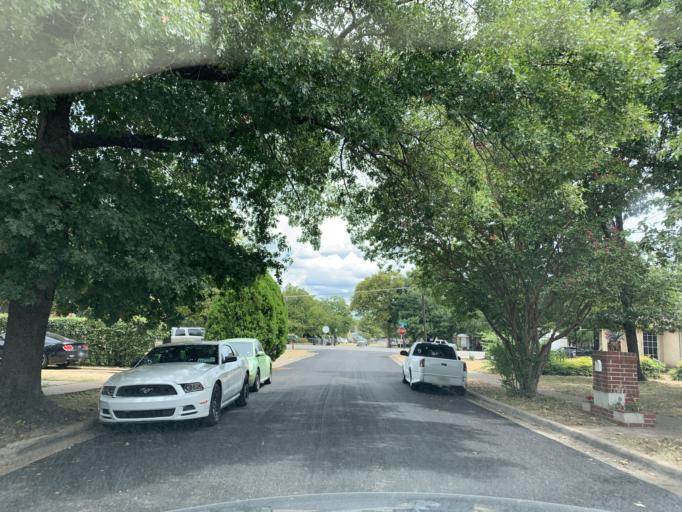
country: US
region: Texas
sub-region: Dallas County
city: Cockrell Hill
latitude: 32.7435
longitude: -96.8814
